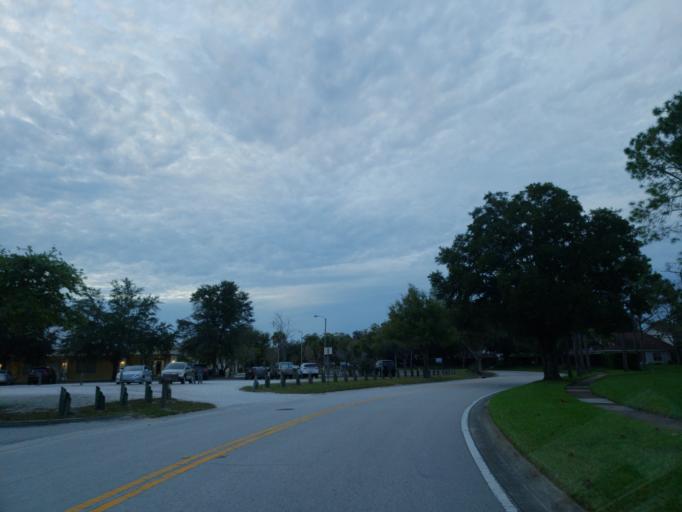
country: US
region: Florida
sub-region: Hillsborough County
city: Lutz
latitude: 28.1797
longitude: -82.4628
